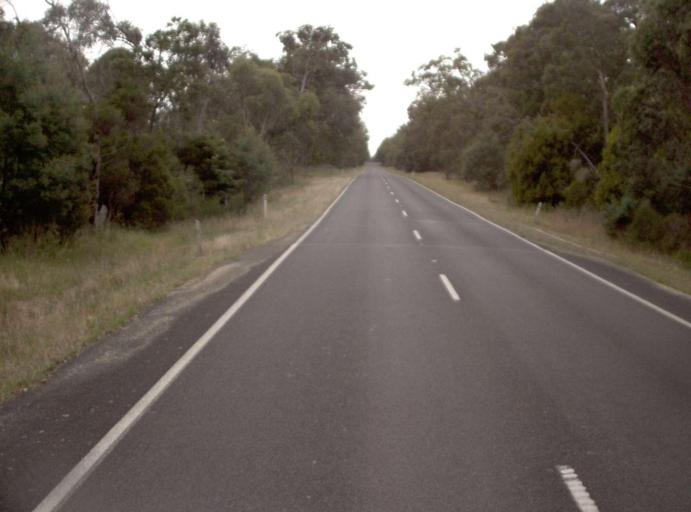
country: AU
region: Victoria
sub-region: Latrobe
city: Traralgon
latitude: -38.5419
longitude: 146.8384
